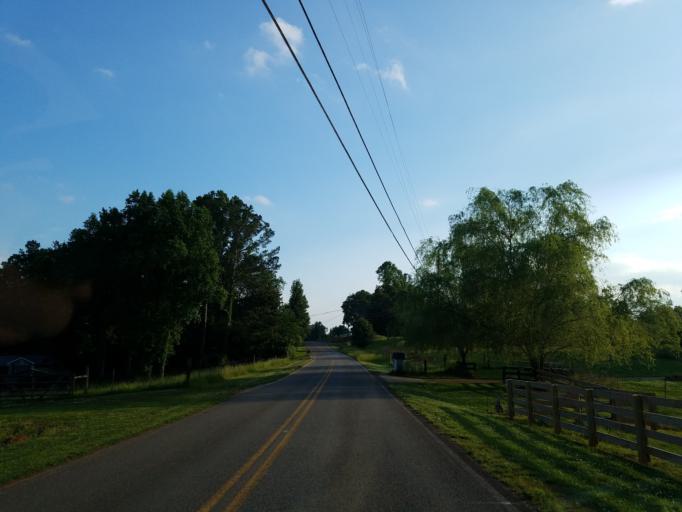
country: US
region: Georgia
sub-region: Cherokee County
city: Ball Ground
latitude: 34.3237
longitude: -84.3695
